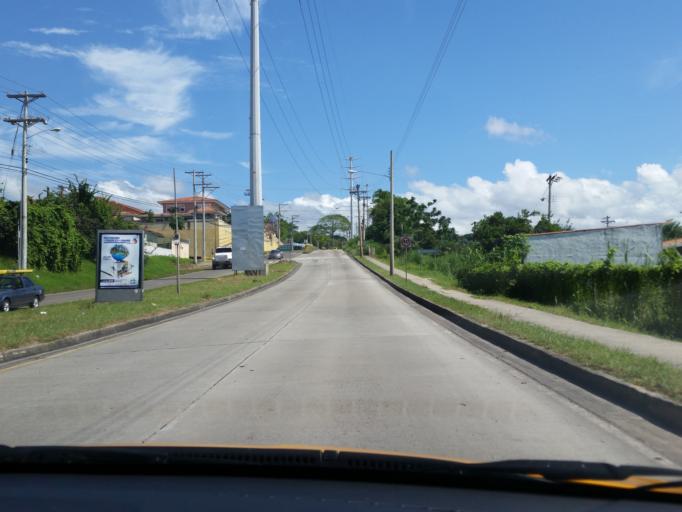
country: PA
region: Panama
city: San Miguelito
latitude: 9.0574
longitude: -79.4617
